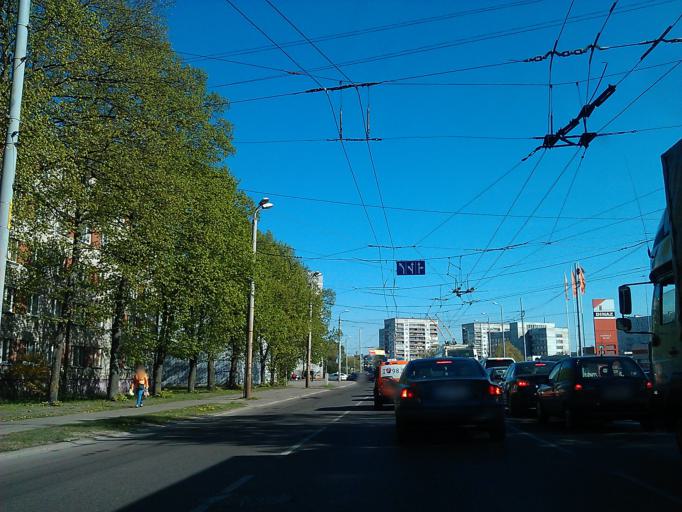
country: LV
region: Riga
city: Riga
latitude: 56.9612
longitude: 24.1736
